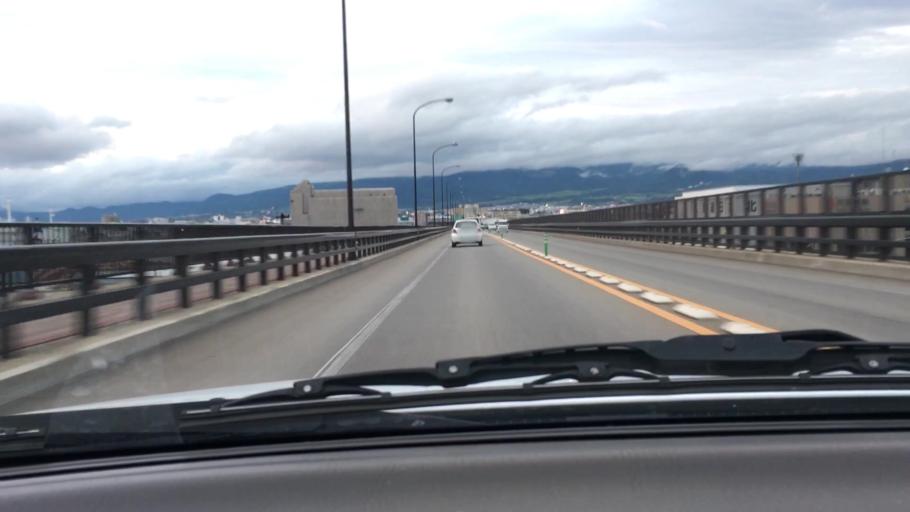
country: JP
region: Hokkaido
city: Hakodate
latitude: 41.7815
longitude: 140.7266
